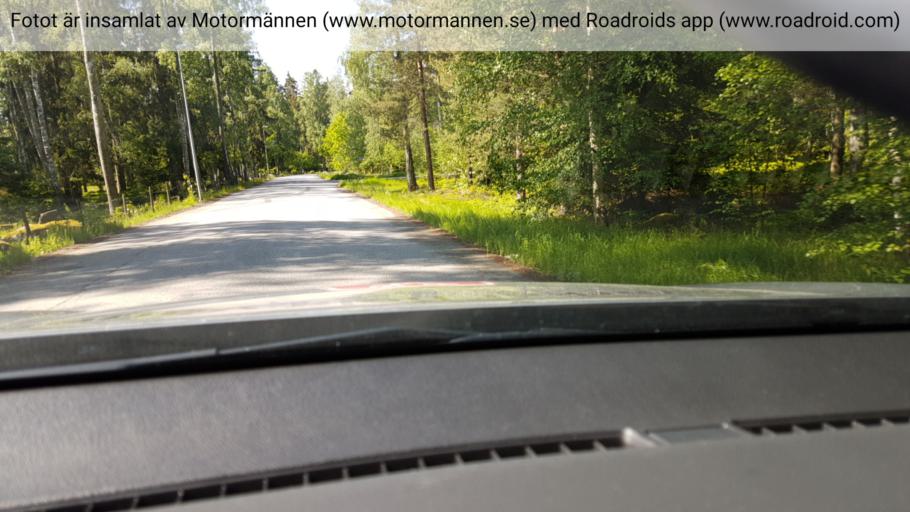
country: SE
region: Vaestra Goetaland
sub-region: Tibro Kommun
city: Tibro
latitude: 58.4234
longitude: 14.1456
